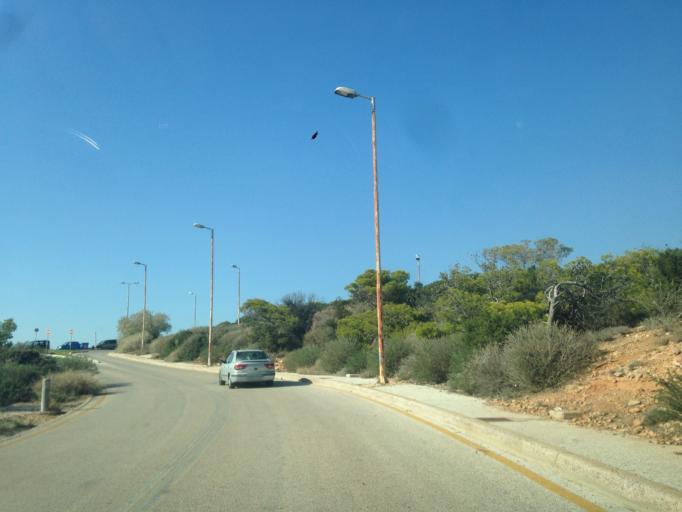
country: GR
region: Attica
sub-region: Nomarchia Anatolikis Attikis
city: Vouliagmeni
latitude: 37.7988
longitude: 23.7731
